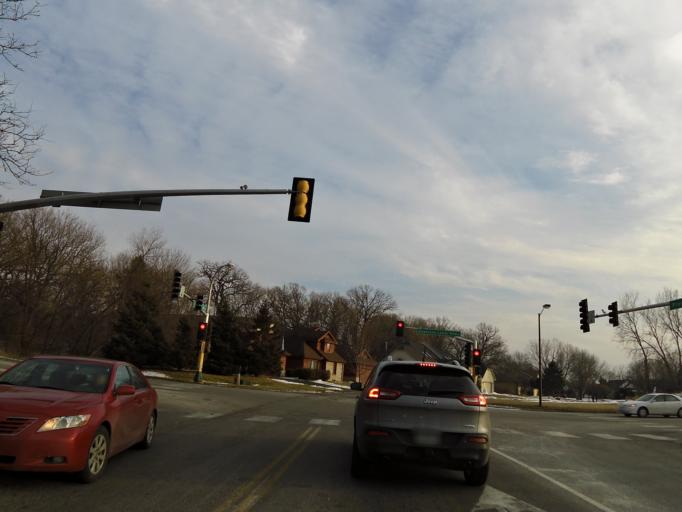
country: US
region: Minnesota
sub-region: Hennepin County
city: Eden Prairie
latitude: 44.8439
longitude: -93.4239
